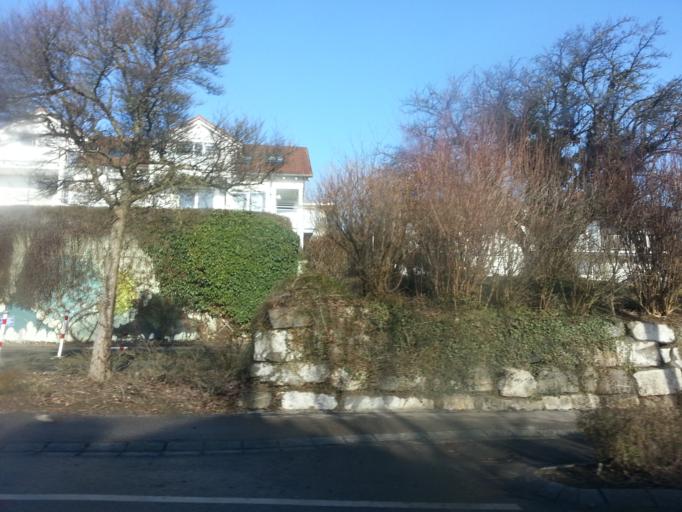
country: DE
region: Baden-Wuerttemberg
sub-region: Tuebingen Region
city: Immenstaad am Bodensee
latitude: 47.6666
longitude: 9.3749
